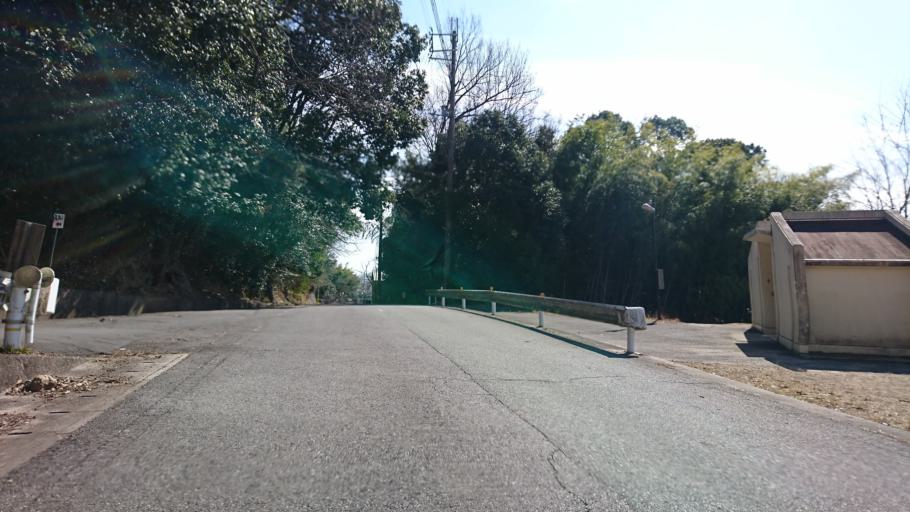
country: JP
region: Hyogo
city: Kakogawacho-honmachi
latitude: 34.8294
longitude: 134.8108
